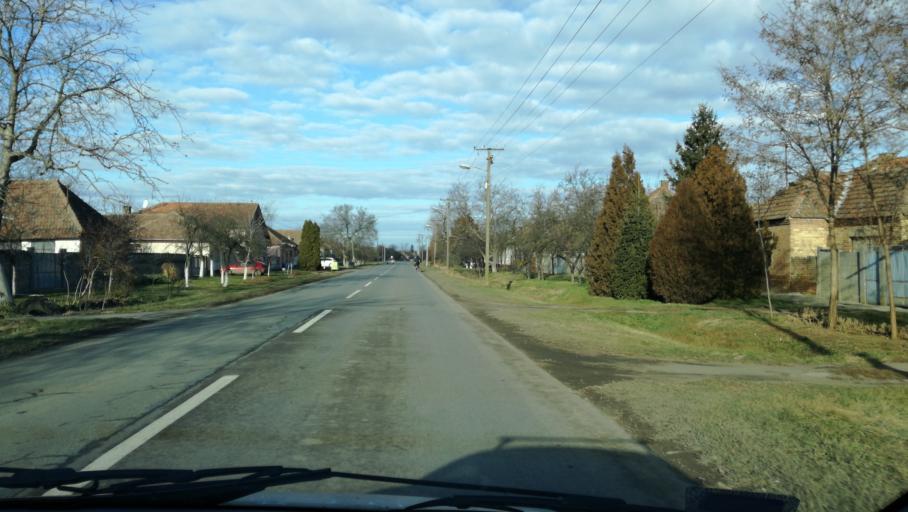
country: RS
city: Ostojicevo
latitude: 45.8921
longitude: 20.1625
